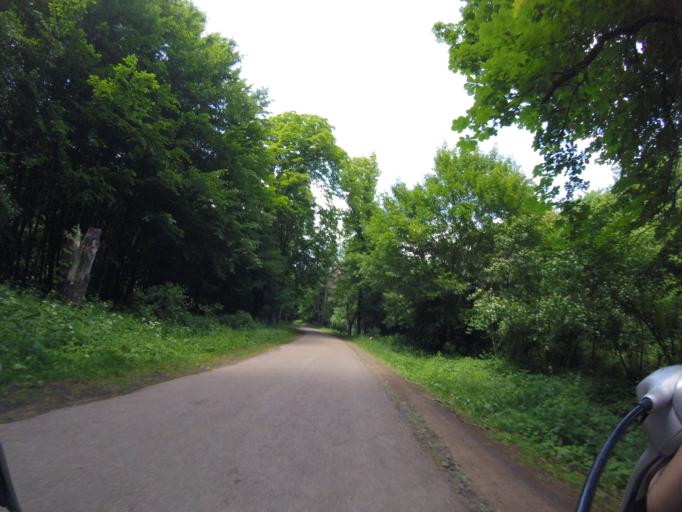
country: HU
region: Heves
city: Parad
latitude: 47.9021
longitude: 20.0563
